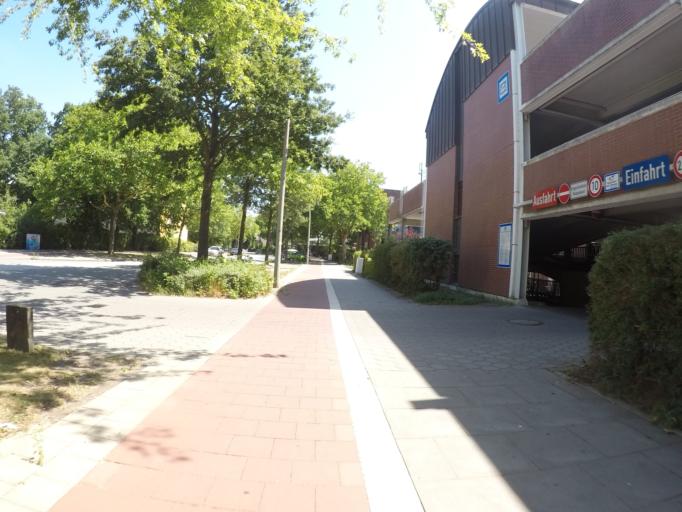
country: DE
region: Lower Saxony
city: Neu Wulmstorf
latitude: 53.4736
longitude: 9.8788
